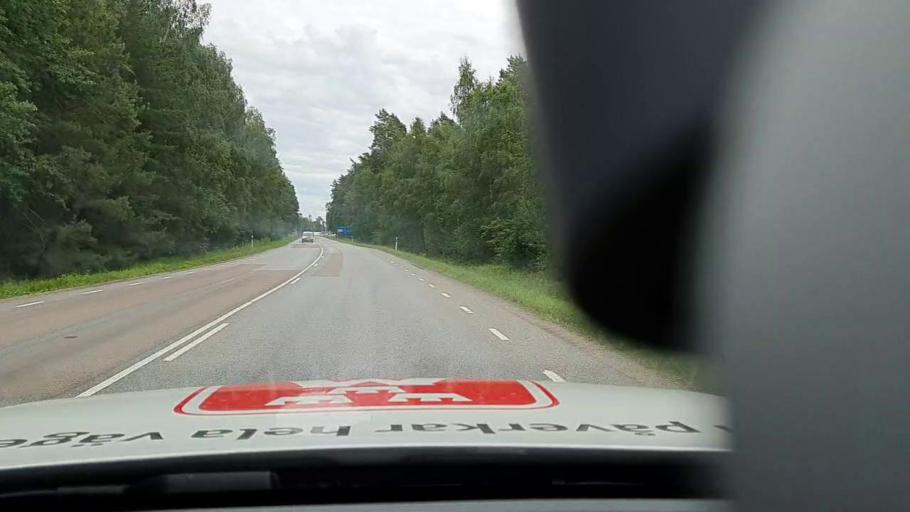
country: SE
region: Vaestra Goetaland
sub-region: Lidkopings Kommun
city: Lidkoping
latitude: 58.4955
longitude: 13.1343
